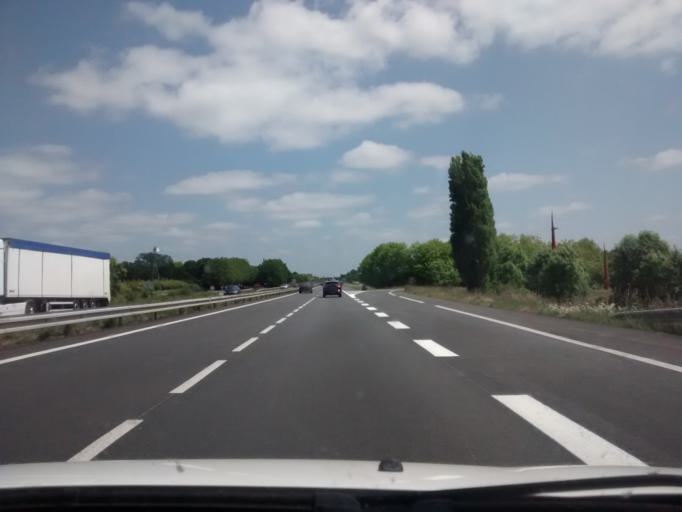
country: FR
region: Pays de la Loire
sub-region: Departement de la Mayenne
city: Vaiges
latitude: 48.0593
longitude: -0.5074
